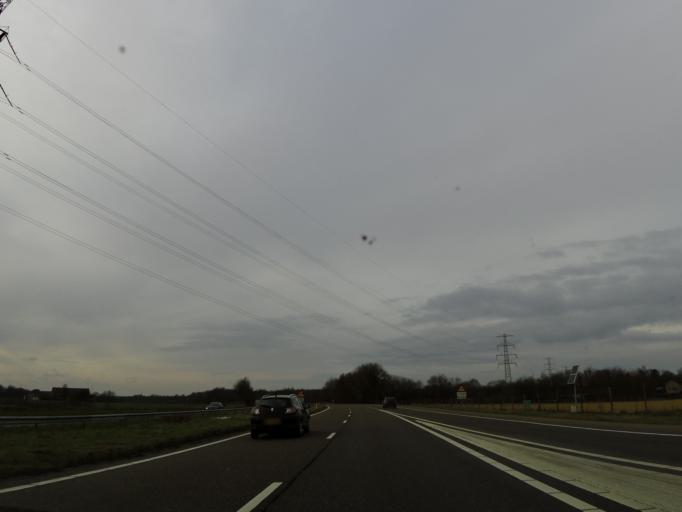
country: NL
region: Limburg
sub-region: Valkenburg aan de Geul
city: Valkenburg
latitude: 50.8826
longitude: 5.8448
